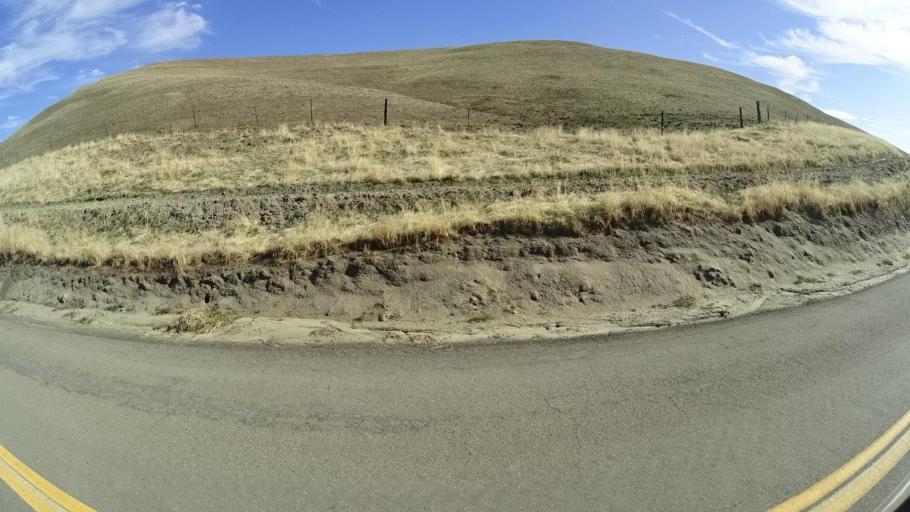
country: US
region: California
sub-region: Kern County
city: Oildale
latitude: 35.6155
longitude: -118.9439
